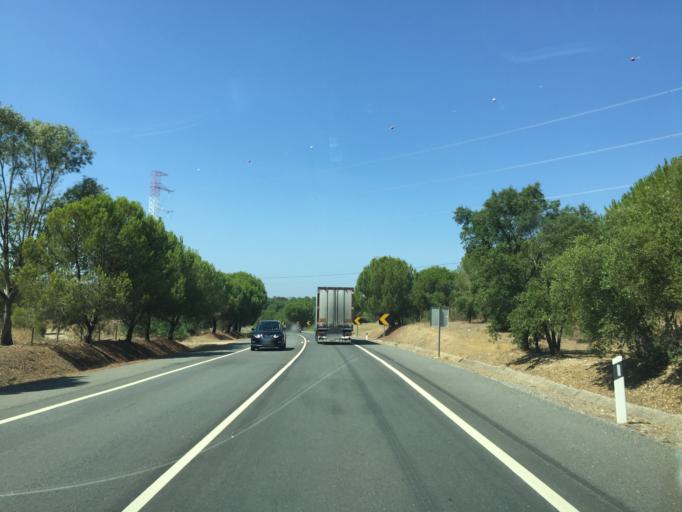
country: PT
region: Faro
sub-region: Silves
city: Sao Bartolomeu de Messines
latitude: 37.2747
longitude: -8.2844
